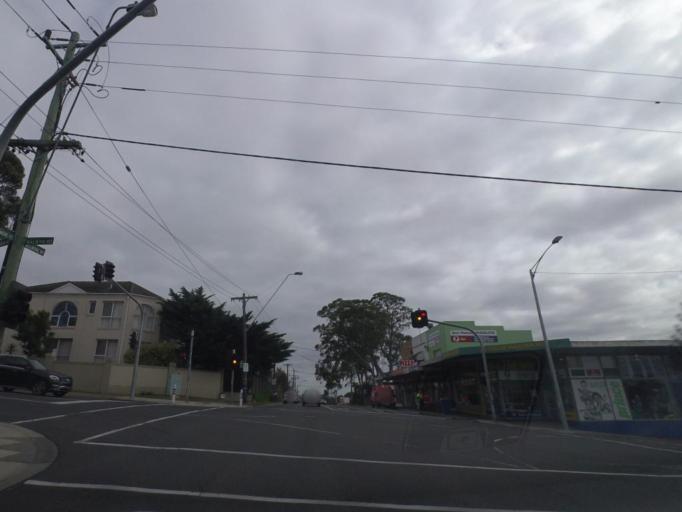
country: AU
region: Victoria
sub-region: Boroondara
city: Balwyn North
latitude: -37.8036
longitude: 145.0833
